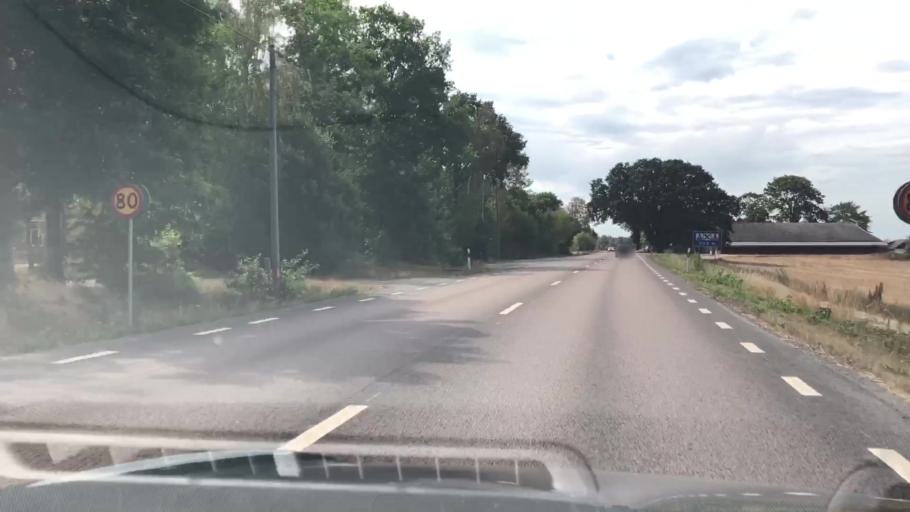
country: SE
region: Kalmar
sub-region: Torsas Kommun
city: Torsas
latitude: 56.3713
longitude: 16.0677
